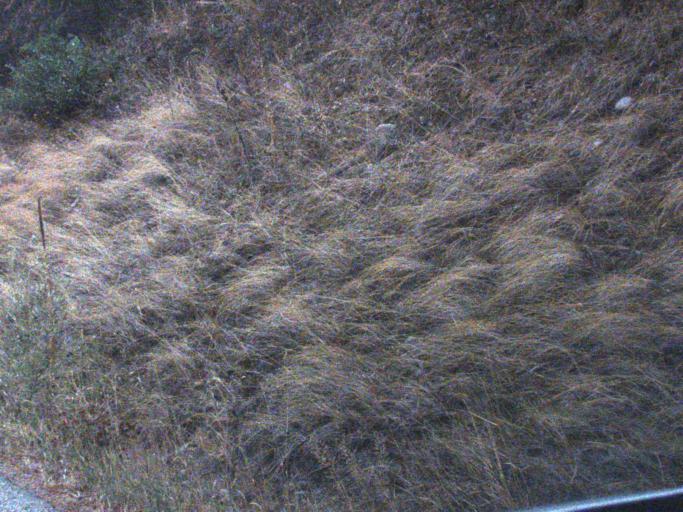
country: CA
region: British Columbia
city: Grand Forks
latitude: 48.9073
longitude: -118.2052
